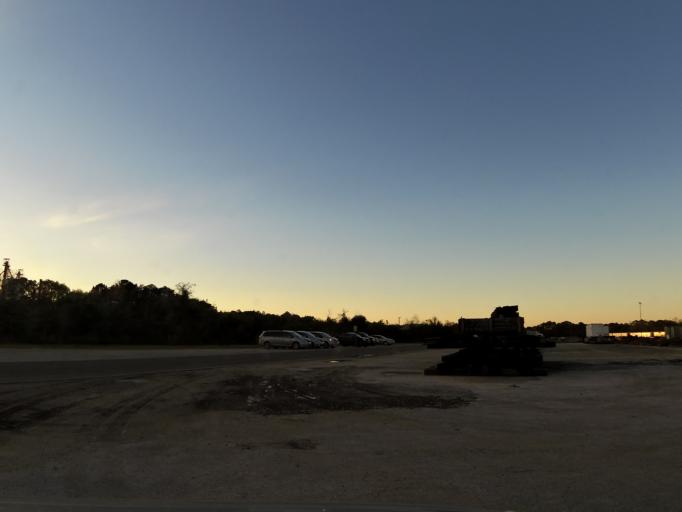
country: US
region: Florida
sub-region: Duval County
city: Jacksonville
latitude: 30.3478
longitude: -81.7085
